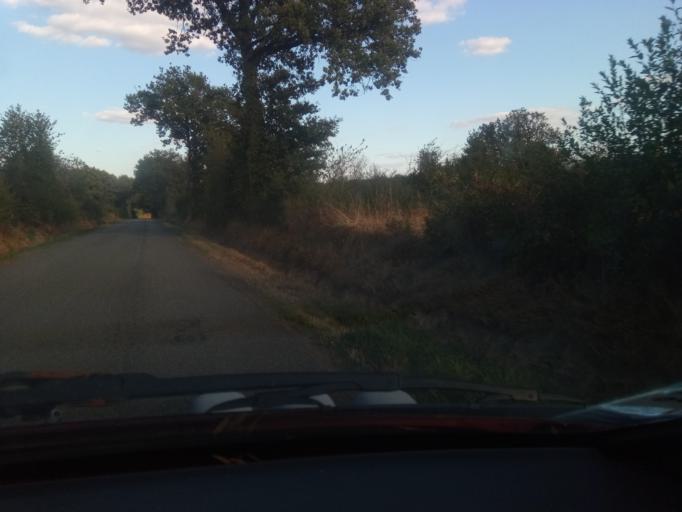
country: FR
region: Poitou-Charentes
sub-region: Departement de la Vienne
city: Availles-Limouzine
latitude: 46.1291
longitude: 0.7136
